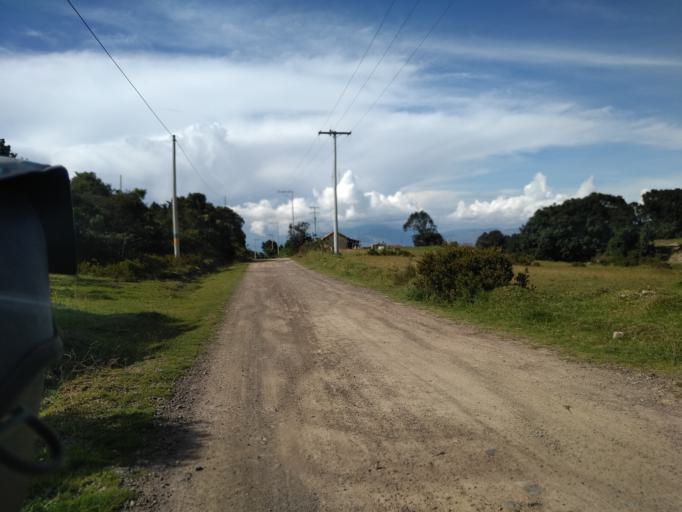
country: CO
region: Boyaca
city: Raquira
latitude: 5.4681
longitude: -73.6377
